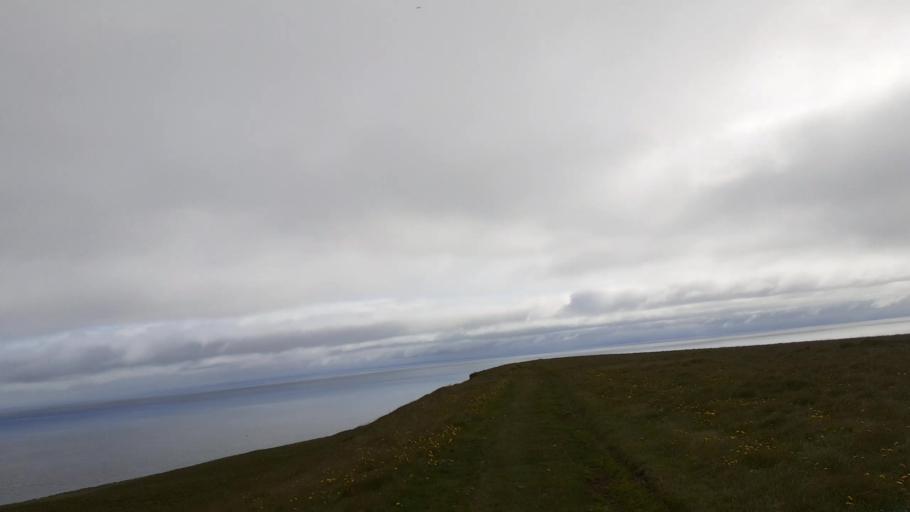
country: IS
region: Northeast
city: Dalvik
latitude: 66.5388
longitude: -17.9827
